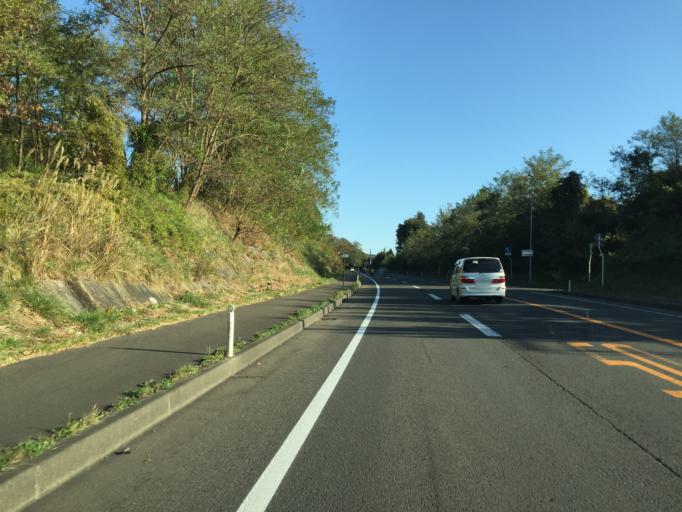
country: JP
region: Fukushima
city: Yanagawamachi-saiwaicho
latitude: 37.8900
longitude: 140.5687
